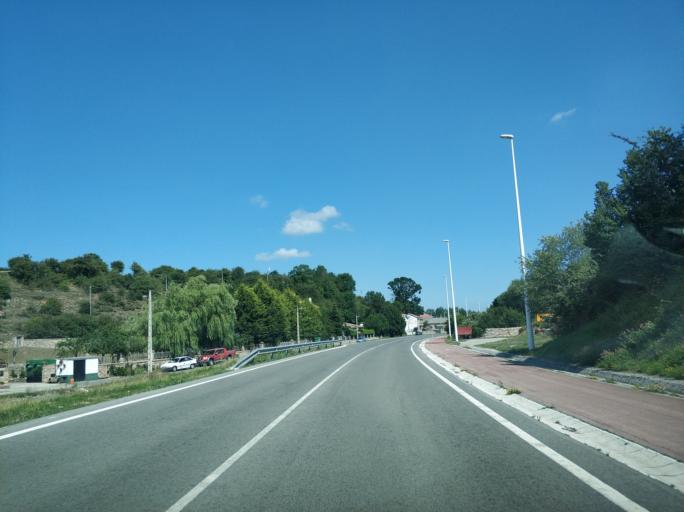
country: ES
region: Cantabria
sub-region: Provincia de Cantabria
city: Villaescusa
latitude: 43.0218
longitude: -4.2295
